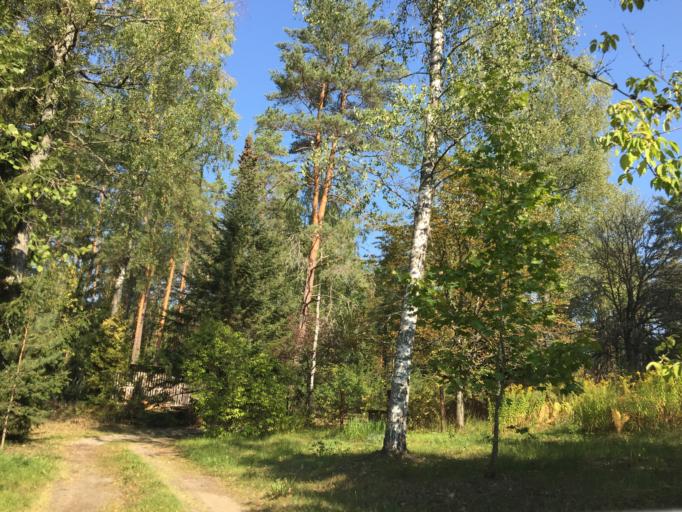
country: LV
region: Incukalns
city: Vangazi
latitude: 57.0978
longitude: 24.5748
